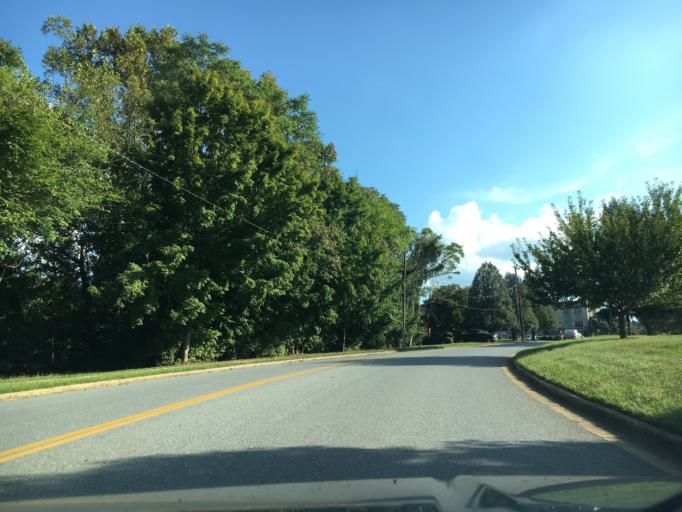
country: US
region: Virginia
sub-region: City of Lynchburg
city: West Lynchburg
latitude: 37.4149
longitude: -79.1693
